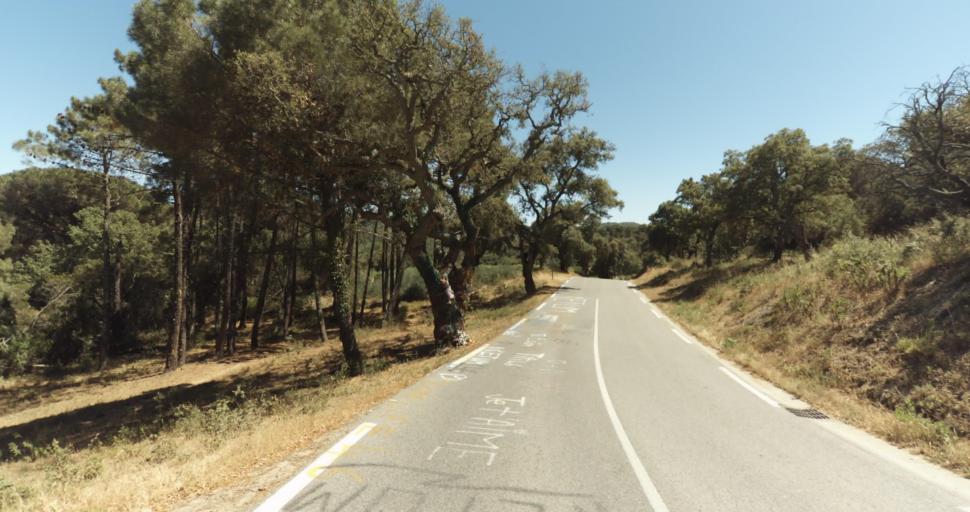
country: FR
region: Provence-Alpes-Cote d'Azur
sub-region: Departement du Var
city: Gassin
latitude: 43.2416
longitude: 6.5629
